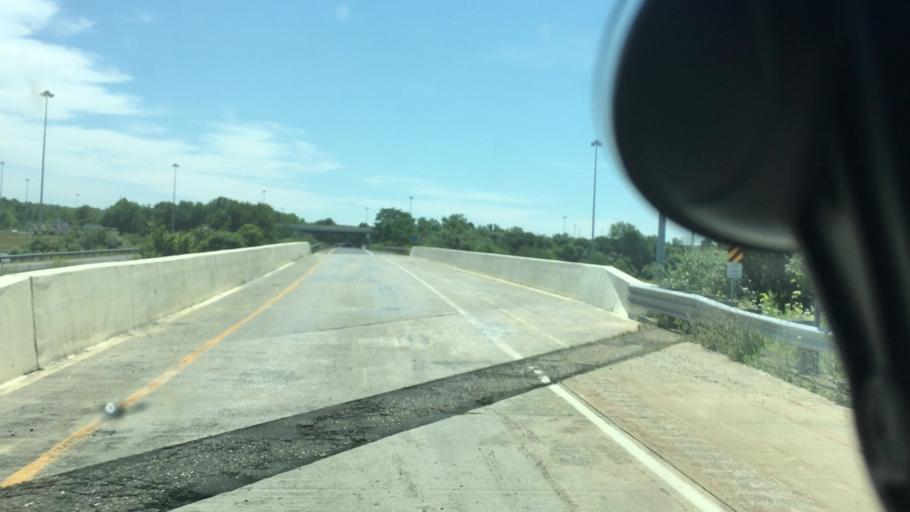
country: US
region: Ohio
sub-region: Trumbull County
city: Mineral Ridge
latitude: 41.1268
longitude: -80.7491
